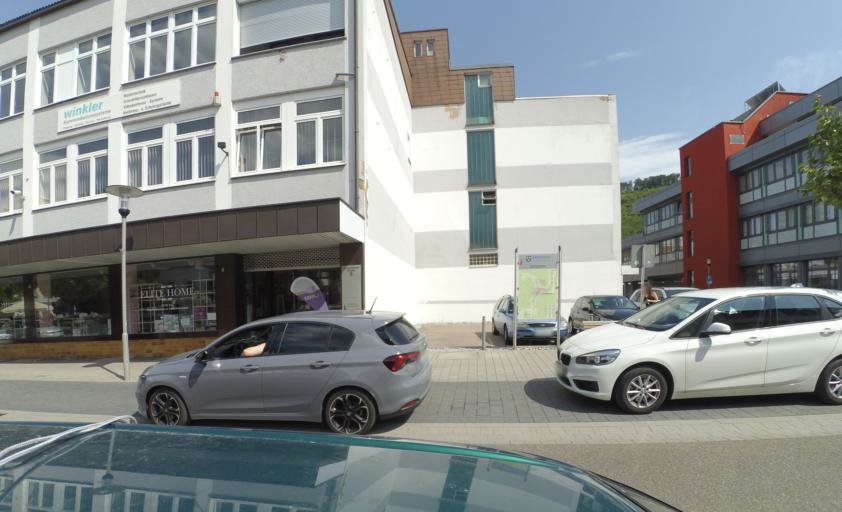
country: DE
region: Baden-Wuerttemberg
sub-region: Regierungsbezirk Stuttgart
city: Oberkochen
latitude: 48.7836
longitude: 10.1052
